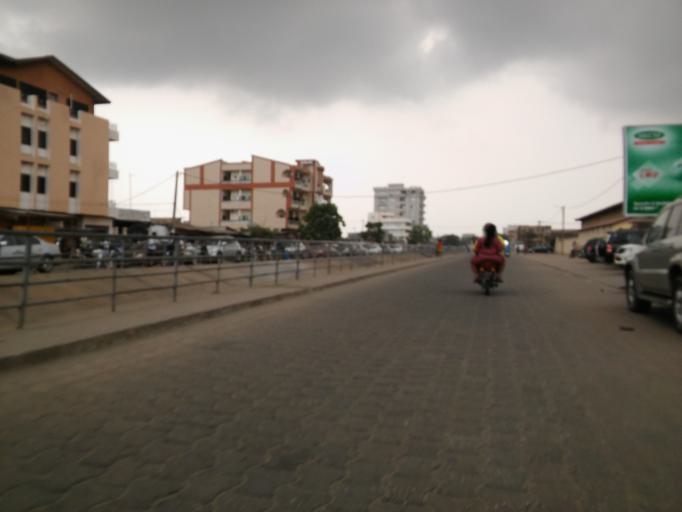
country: BJ
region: Littoral
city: Cotonou
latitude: 6.3765
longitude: 2.4161
